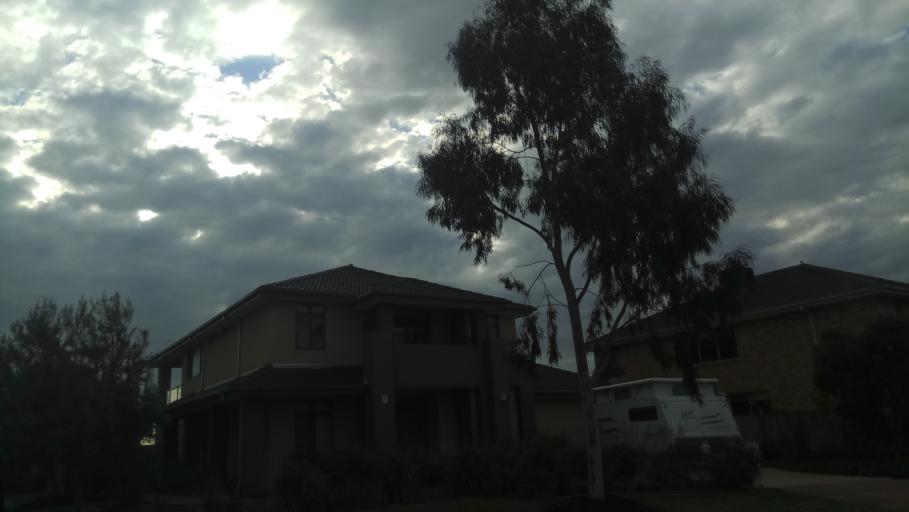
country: AU
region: Victoria
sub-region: Hobsons Bay
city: Altona Meadows
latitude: -37.8962
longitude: 144.7738
